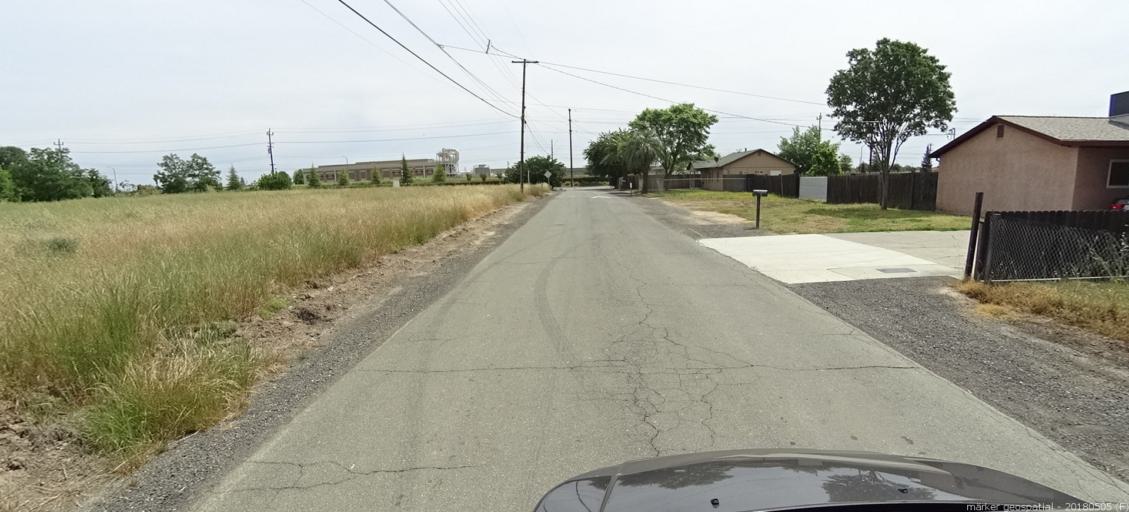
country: US
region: California
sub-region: Sacramento County
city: Arden-Arcade
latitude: 38.6435
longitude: -121.4122
